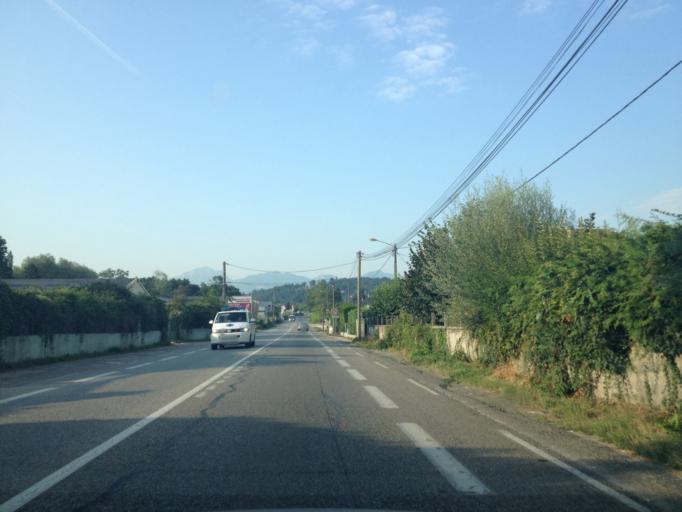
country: FR
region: Rhone-Alpes
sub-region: Departement de la Savoie
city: Viviers-du-Lac
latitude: 45.6578
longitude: 5.9087
